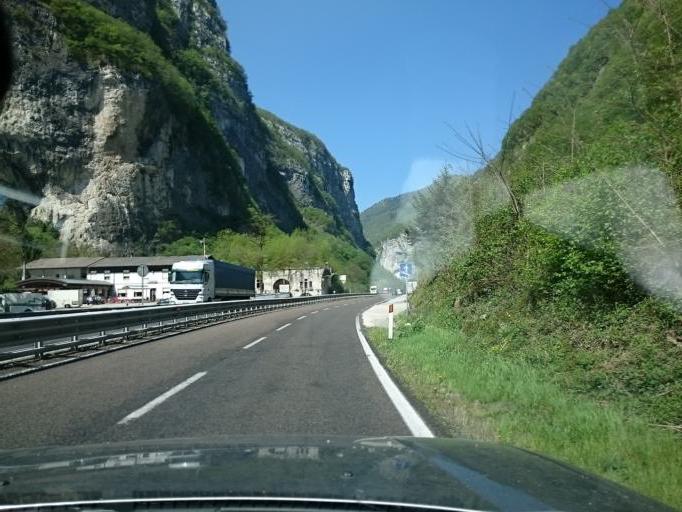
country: IT
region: Veneto
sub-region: Provincia di Vicenza
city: Cismon del Grappa
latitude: 45.9368
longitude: 11.7254
